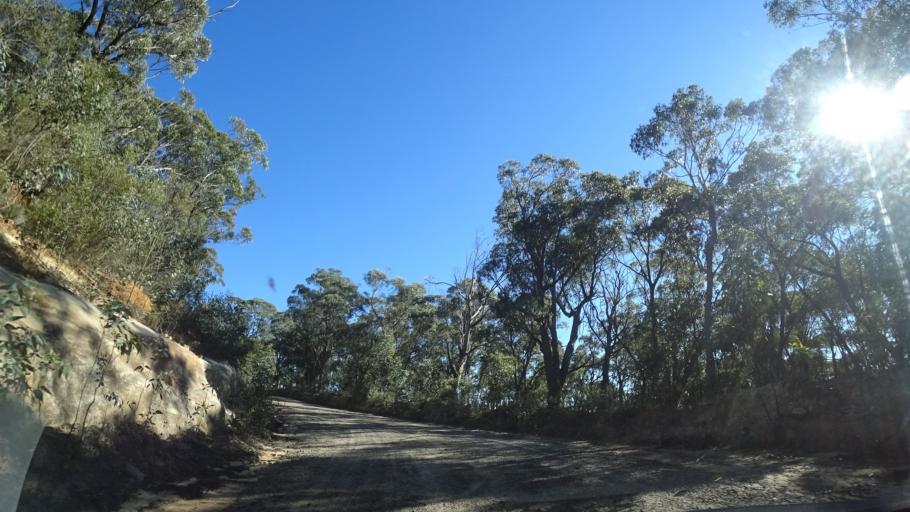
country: AU
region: New South Wales
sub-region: Lithgow
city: Lithgow
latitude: -33.4906
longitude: 150.2679
